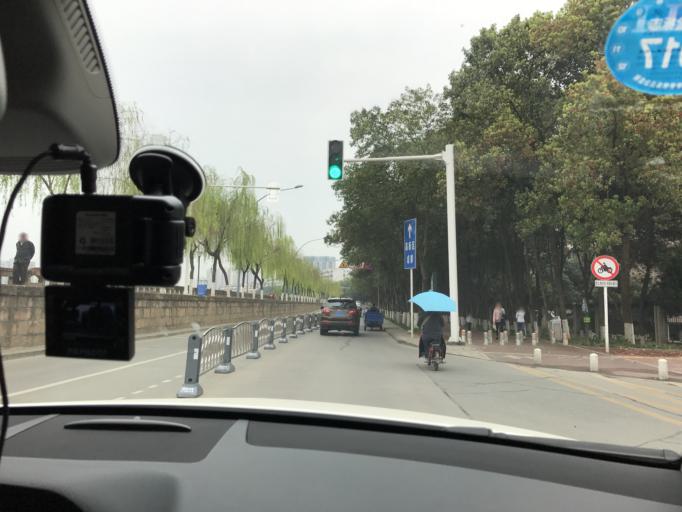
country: CN
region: Sichuan
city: Mianyang
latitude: 31.4563
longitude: 104.7066
